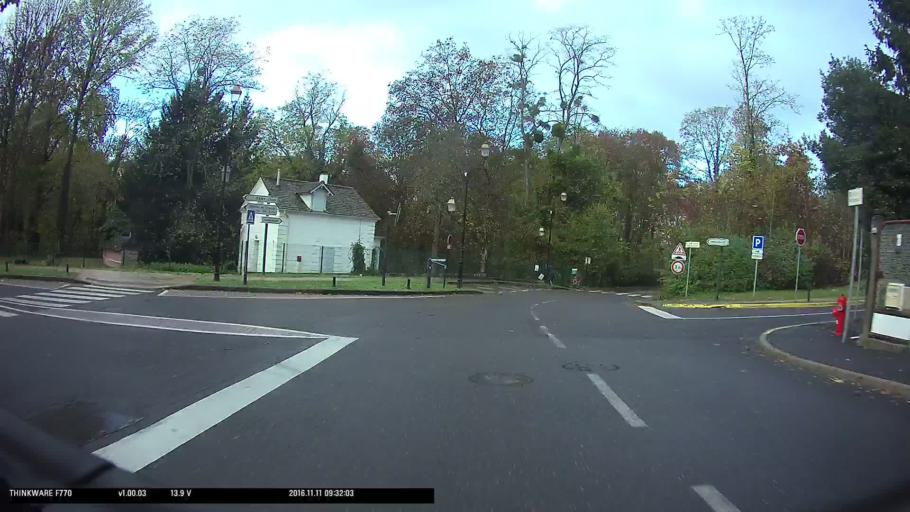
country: FR
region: Ile-de-France
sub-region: Departement du Val-d'Oise
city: Osny
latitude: 49.0653
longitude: 2.0655
